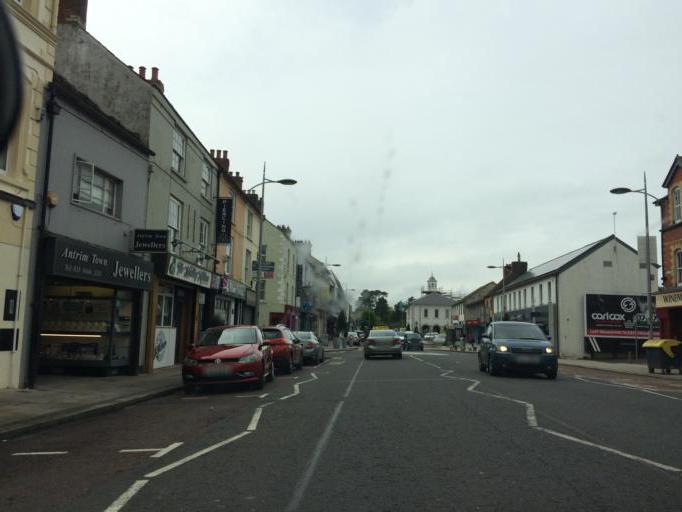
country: GB
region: Northern Ireland
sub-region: Antrim Borough
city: Antrim
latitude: 54.7144
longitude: -6.2187
